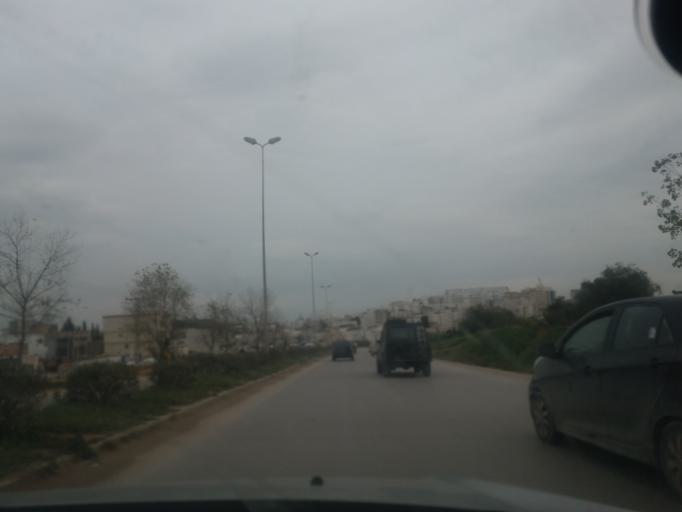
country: TN
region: Tunis
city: Tunis
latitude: 36.8543
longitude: 10.1344
